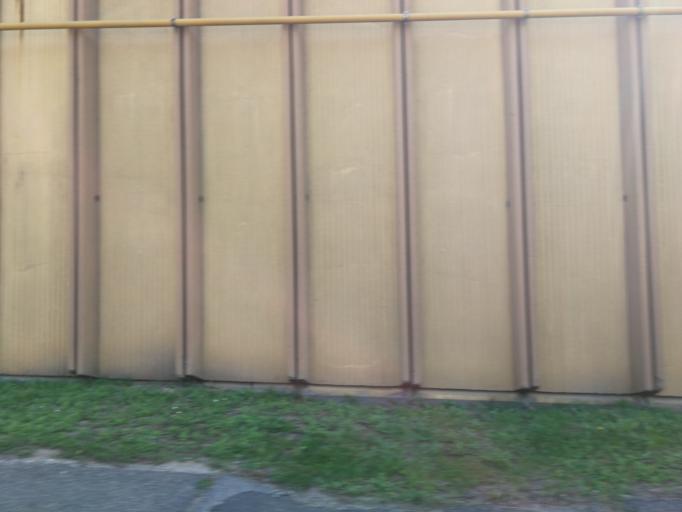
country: HU
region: Vas
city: Sarvar
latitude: 47.2566
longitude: 16.9248
